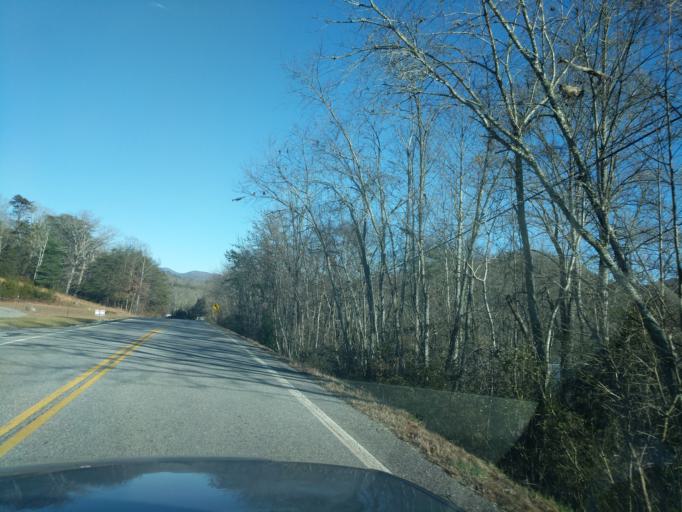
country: US
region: Georgia
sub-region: Towns County
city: Hiawassee
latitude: 34.9217
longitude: -83.6959
